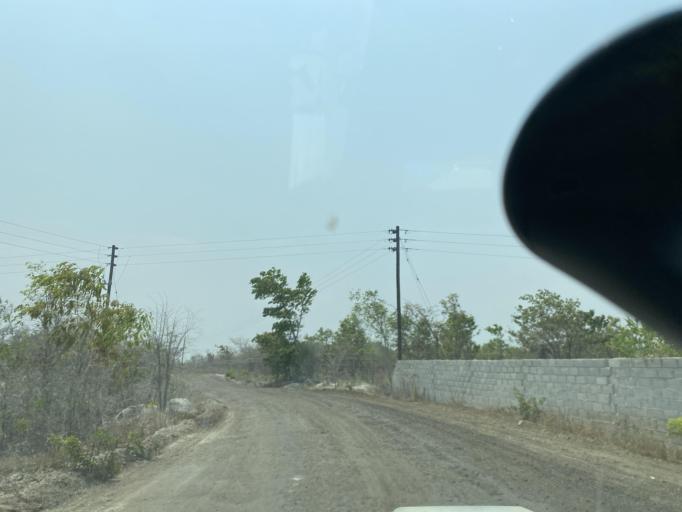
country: ZM
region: Lusaka
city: Lusaka
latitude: -15.5326
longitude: 28.4478
